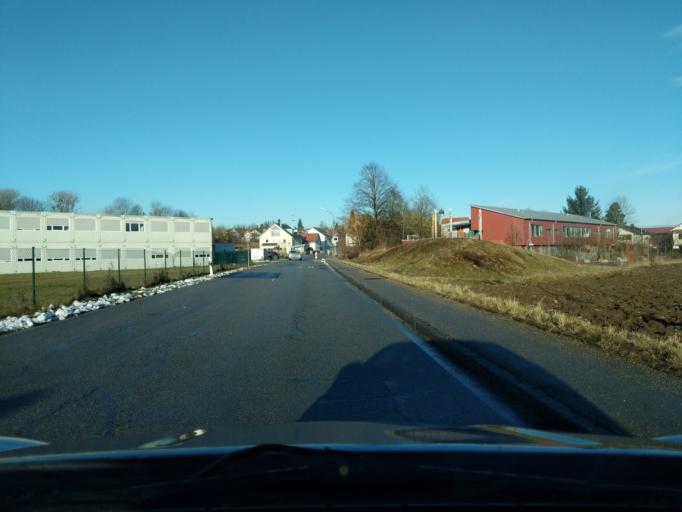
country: DE
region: Bavaria
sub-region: Upper Bavaria
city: Zorneding
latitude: 48.0925
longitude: 11.8382
